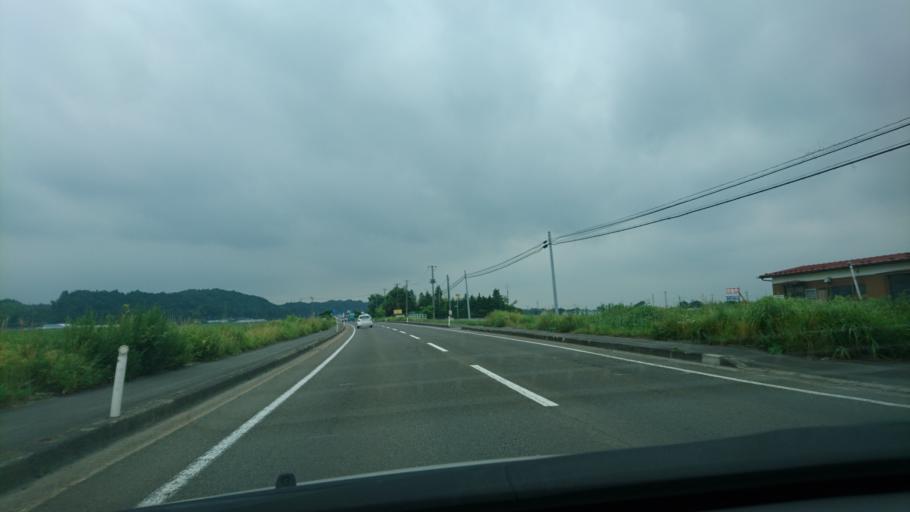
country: JP
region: Miyagi
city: Furukawa
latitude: 38.6620
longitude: 140.8736
